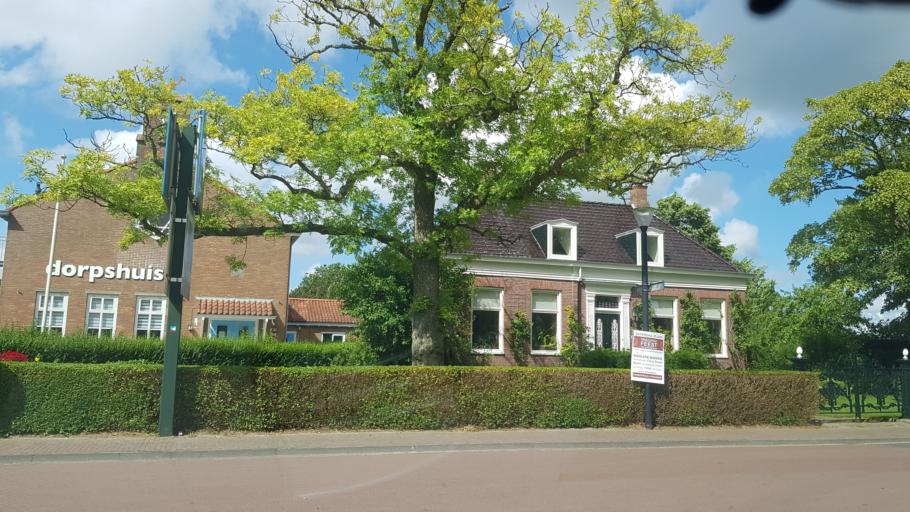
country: NL
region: Groningen
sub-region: Gemeente Winsum
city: Winsum
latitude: 53.3998
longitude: 6.4548
